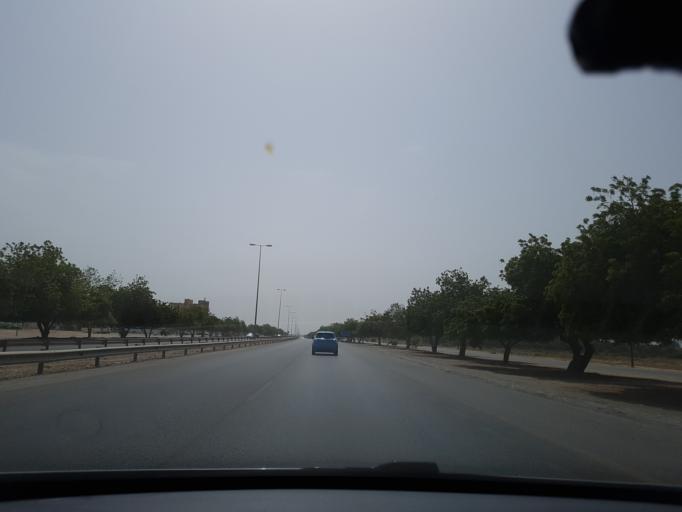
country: OM
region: Al Batinah
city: As Suwayq
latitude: 23.8052
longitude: 57.4727
